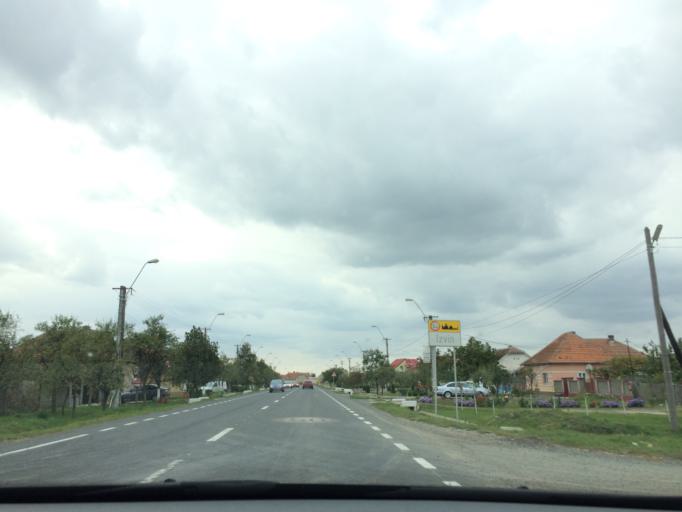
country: RO
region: Timis
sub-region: Oras Recas
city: Izvin
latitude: 45.8022
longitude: 21.4714
